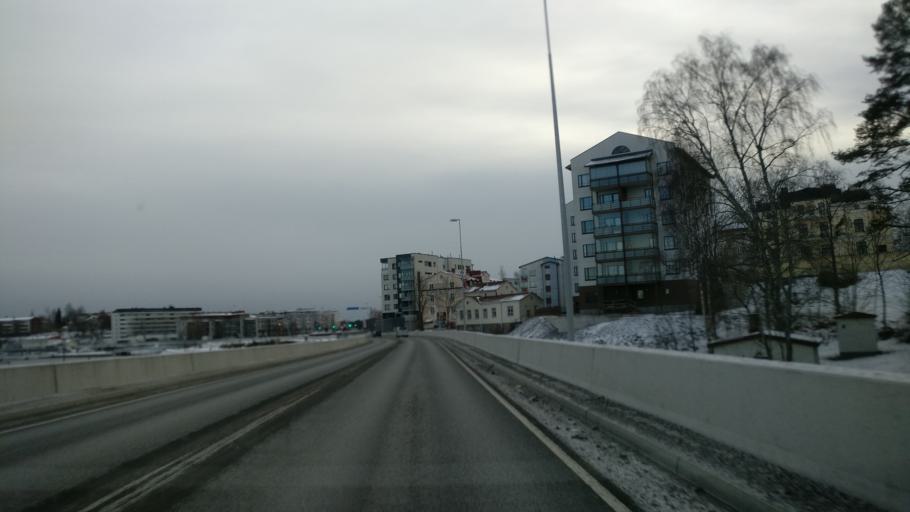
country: FI
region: Southern Savonia
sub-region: Savonlinna
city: Savonlinna
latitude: 61.8724
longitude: 28.8815
